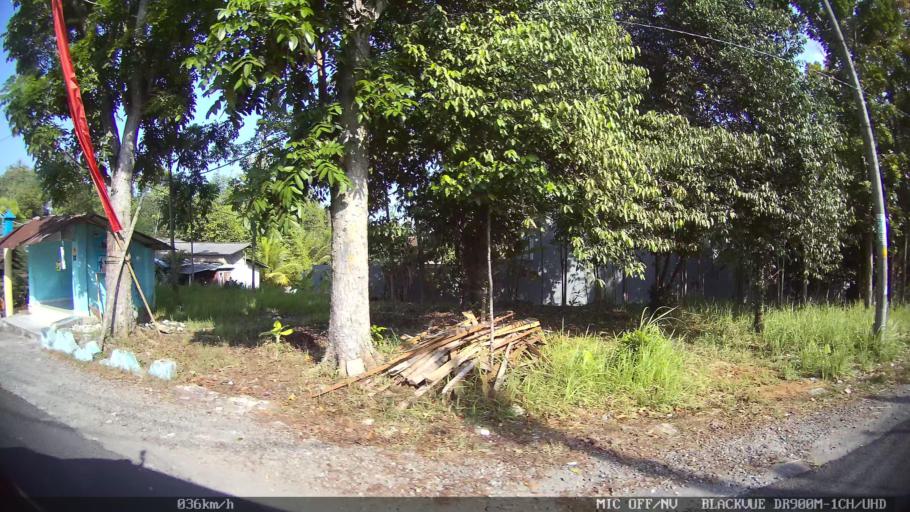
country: ID
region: Daerah Istimewa Yogyakarta
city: Godean
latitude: -7.8139
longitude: 110.2760
